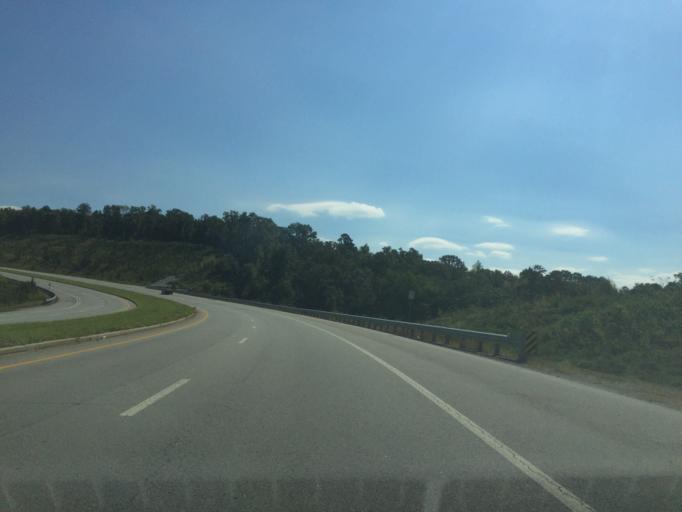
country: US
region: Tennessee
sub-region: Hamilton County
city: Harrison
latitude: 35.0730
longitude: -85.1246
